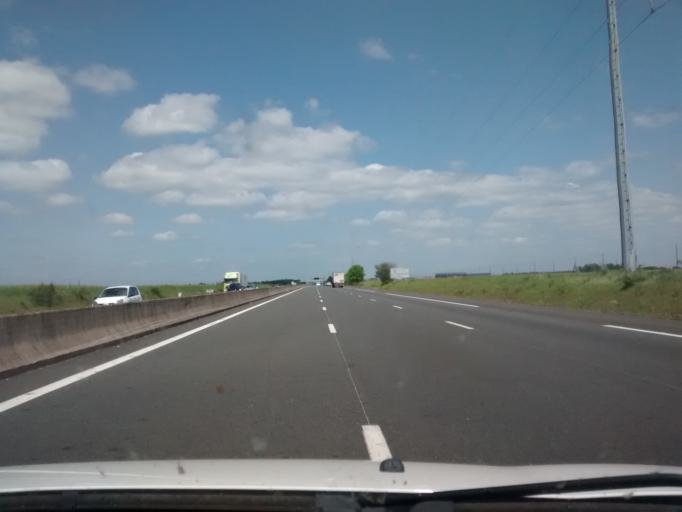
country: FR
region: Centre
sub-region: Departement d'Eure-et-Loir
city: Dammarie
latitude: 48.3462
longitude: 1.4150
